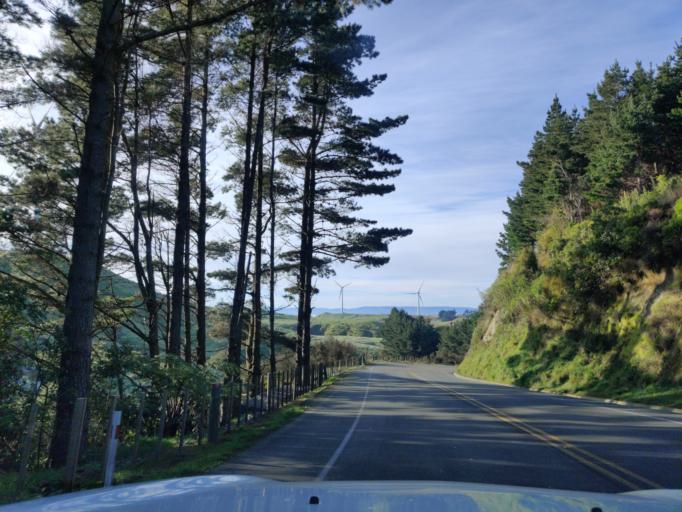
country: NZ
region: Manawatu-Wanganui
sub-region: Palmerston North City
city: Palmerston North
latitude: -40.2955
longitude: 175.8075
